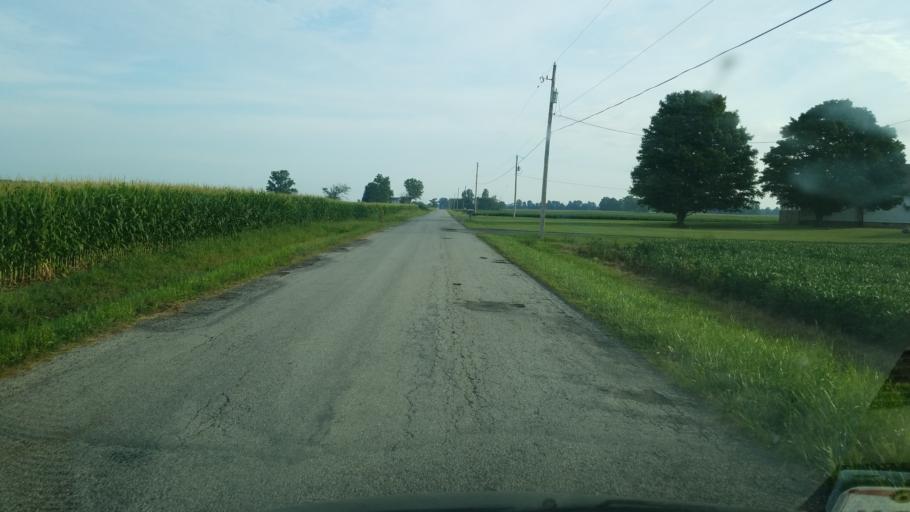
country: US
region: Ohio
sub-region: Morrow County
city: Cardington
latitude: 40.5953
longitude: -82.9186
